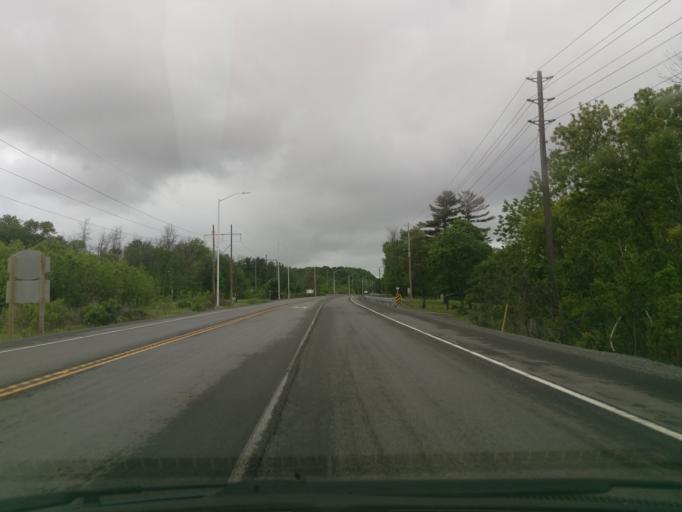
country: CA
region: Ontario
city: Clarence-Rockland
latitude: 45.5167
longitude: -75.4285
